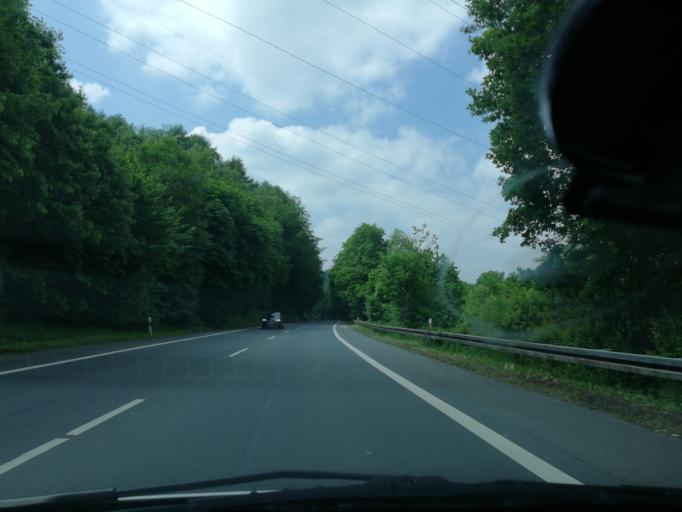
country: DE
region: North Rhine-Westphalia
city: Herdecke
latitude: 51.4182
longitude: 7.4416
